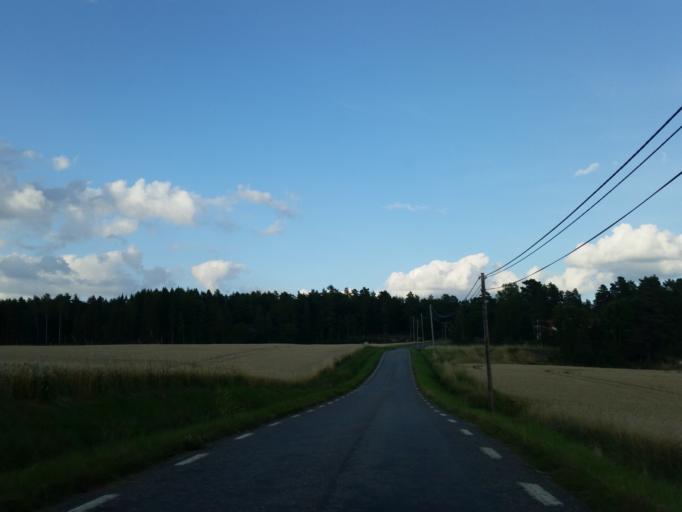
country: SE
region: Stockholm
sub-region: Nykvarns Kommun
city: Nykvarn
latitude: 59.2523
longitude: 17.4113
